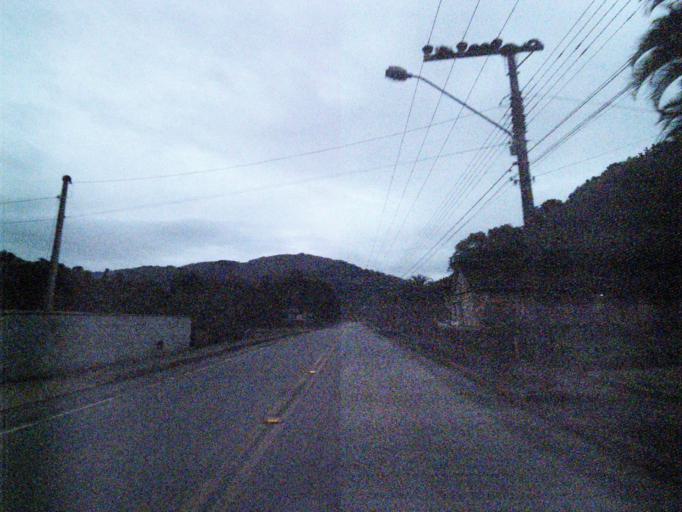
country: BR
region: Santa Catarina
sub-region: Pomerode
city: Pomerode
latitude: -26.7455
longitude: -49.1685
